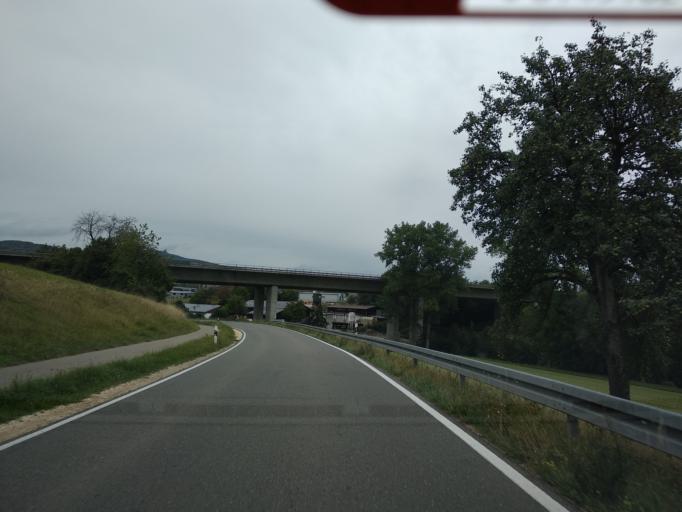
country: DE
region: Baden-Wuerttemberg
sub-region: Freiburg Region
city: Hilzingen
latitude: 47.7550
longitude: 8.7884
